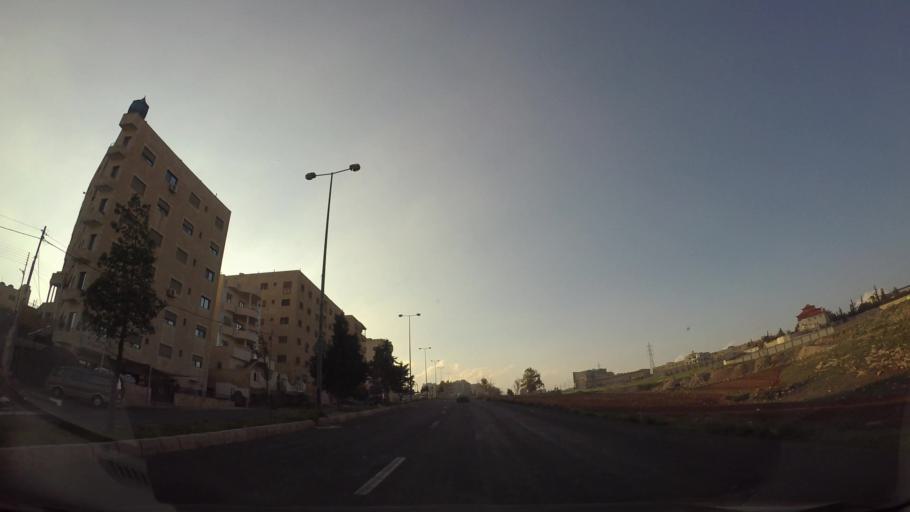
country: JO
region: Amman
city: Amman
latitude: 31.9847
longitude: 35.9548
